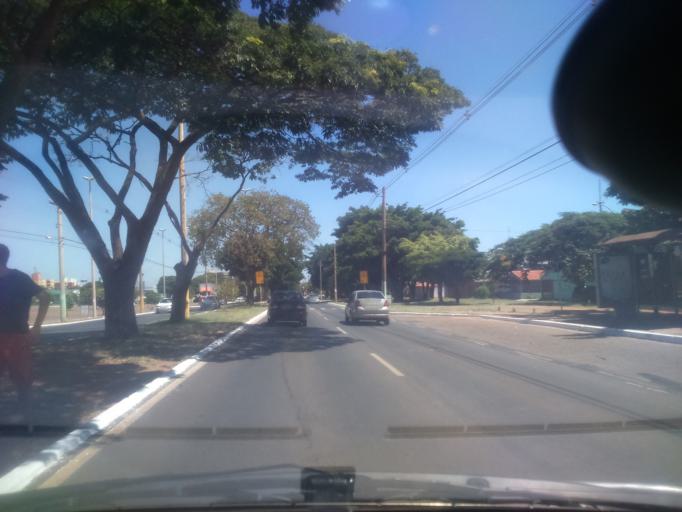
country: BR
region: Federal District
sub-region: Brasilia
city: Brasilia
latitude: -16.0099
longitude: -48.0621
